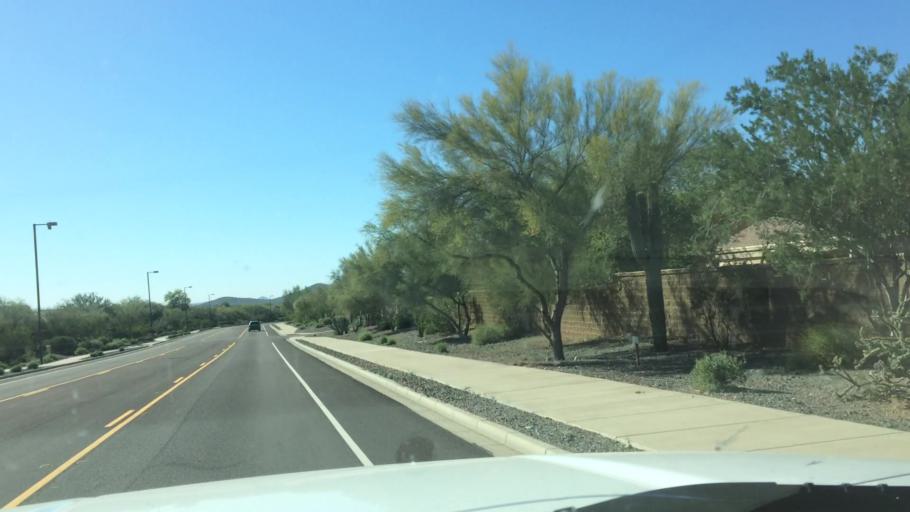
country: US
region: Arizona
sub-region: Maricopa County
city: Anthem
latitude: 33.8504
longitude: -112.1112
